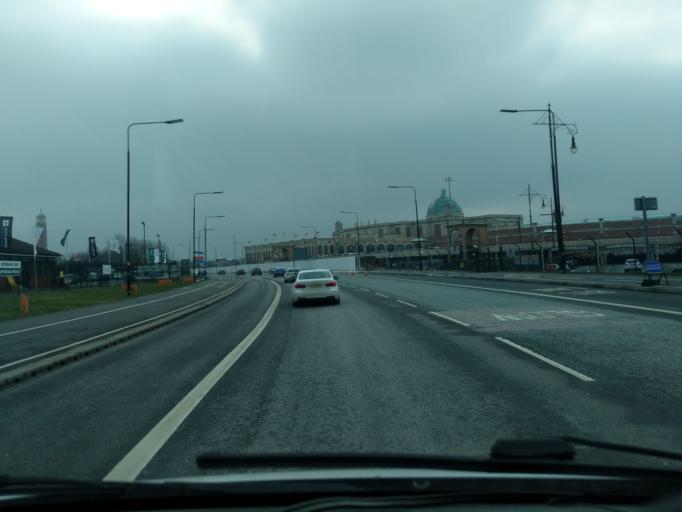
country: GB
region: England
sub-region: City and Borough of Salford
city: Eccles
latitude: 53.4694
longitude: -2.3490
